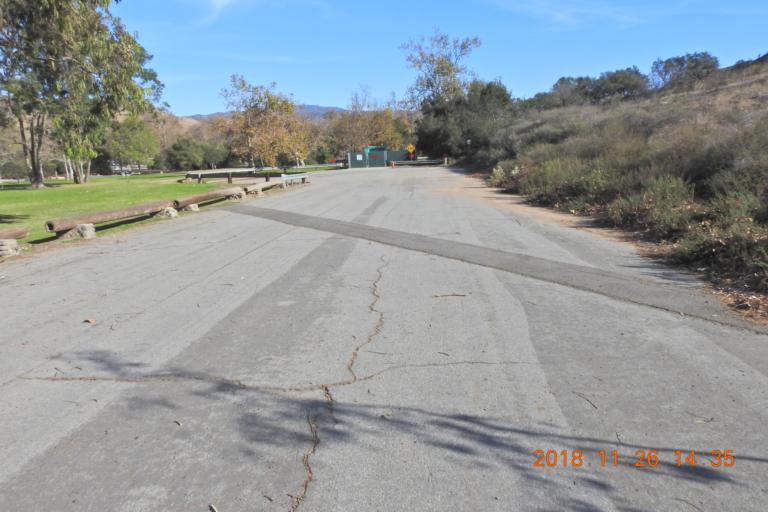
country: US
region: California
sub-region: Orange County
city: North Tustin
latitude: 33.7960
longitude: -117.7567
